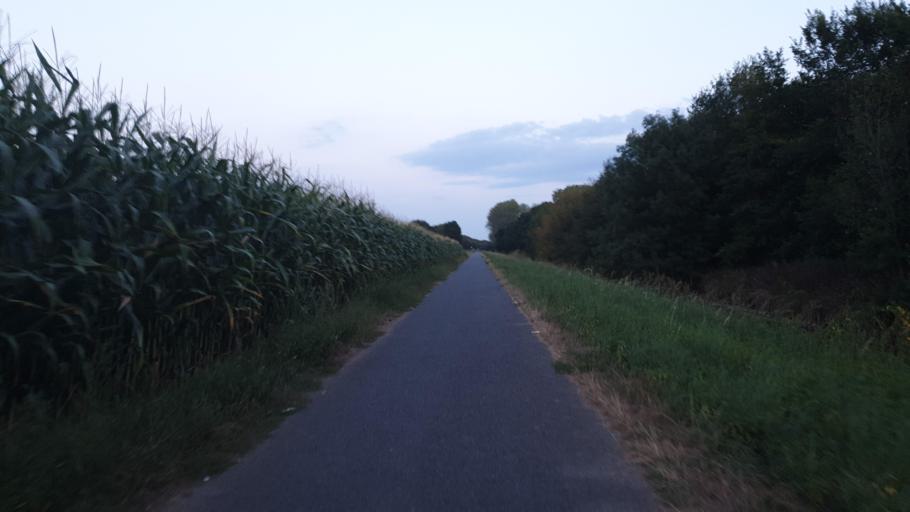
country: DE
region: North Rhine-Westphalia
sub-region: Regierungsbezirk Koln
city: Bergheim
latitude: 50.9373
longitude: 6.6588
